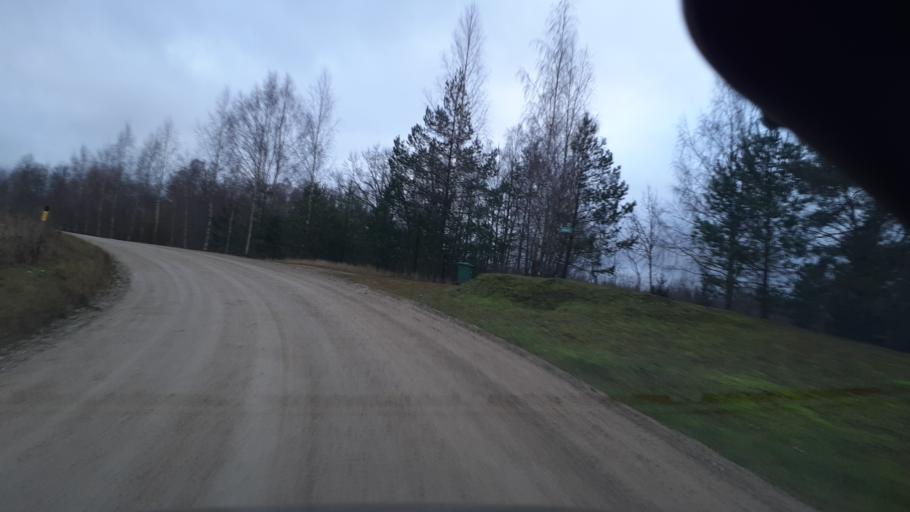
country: LV
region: Alsunga
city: Alsunga
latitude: 56.8798
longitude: 21.6946
